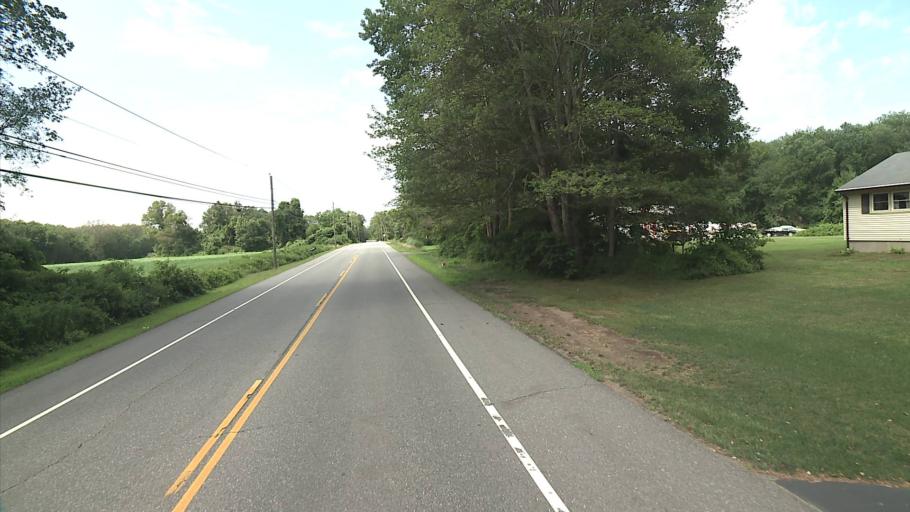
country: US
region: Connecticut
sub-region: New London County
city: Colchester
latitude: 41.5459
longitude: -72.2755
